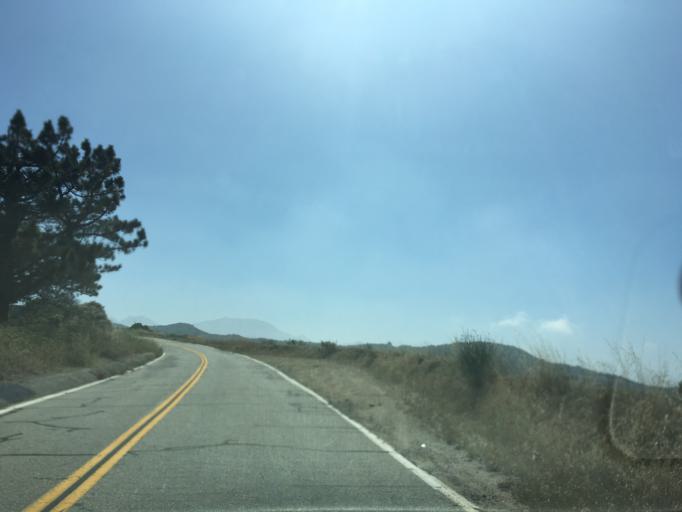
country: US
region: California
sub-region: Los Angeles County
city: Glendora
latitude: 34.1994
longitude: -117.8285
